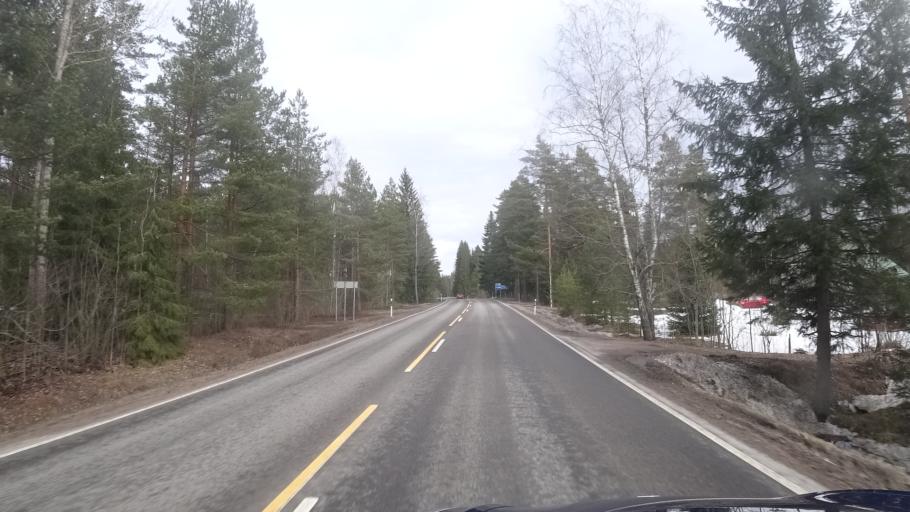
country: FI
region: Kymenlaakso
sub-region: Kouvola
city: Anjala
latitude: 60.6879
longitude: 26.7563
